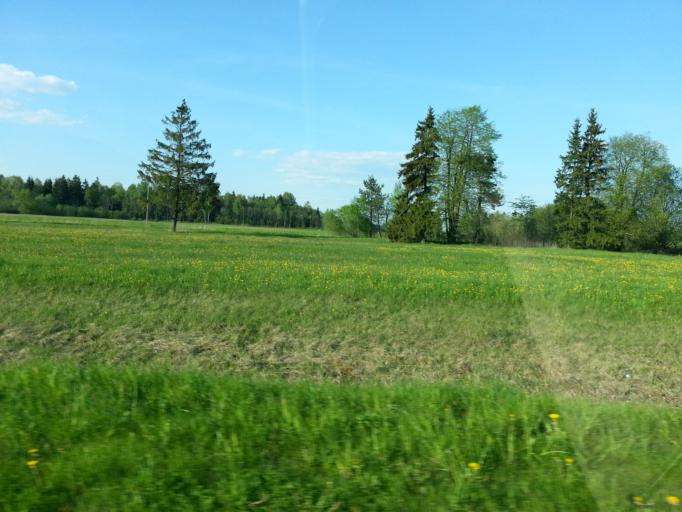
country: LT
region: Vilnius County
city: Ukmerge
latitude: 55.3994
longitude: 24.6945
